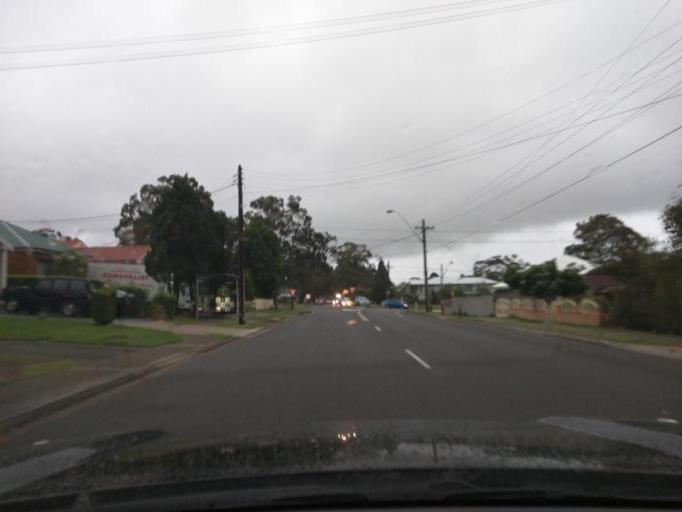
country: AU
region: New South Wales
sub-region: Sutherland Shire
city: Gymea
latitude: -34.0423
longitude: 151.0835
